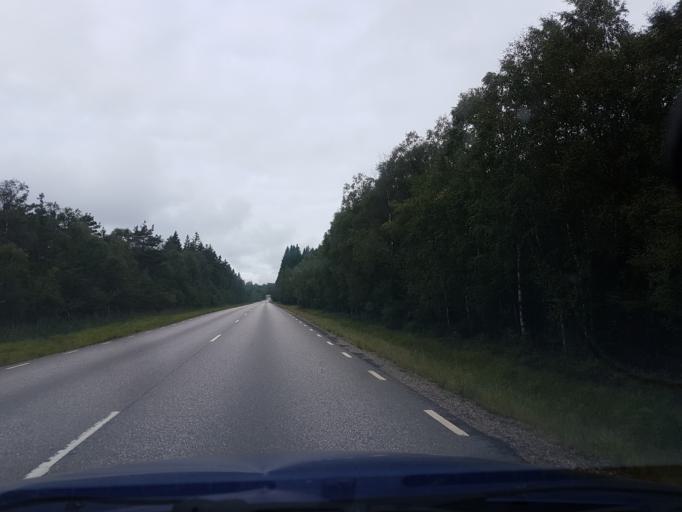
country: SE
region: Vaestra Goetaland
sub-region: Lerums Kommun
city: Grabo
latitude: 57.9219
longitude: 12.2873
